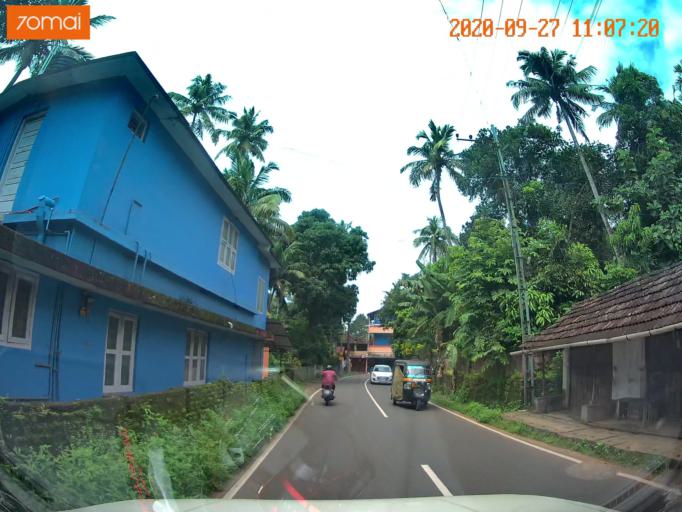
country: IN
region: Kerala
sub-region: Thrissur District
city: Irinjalakuda
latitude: 10.4278
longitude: 76.2371
